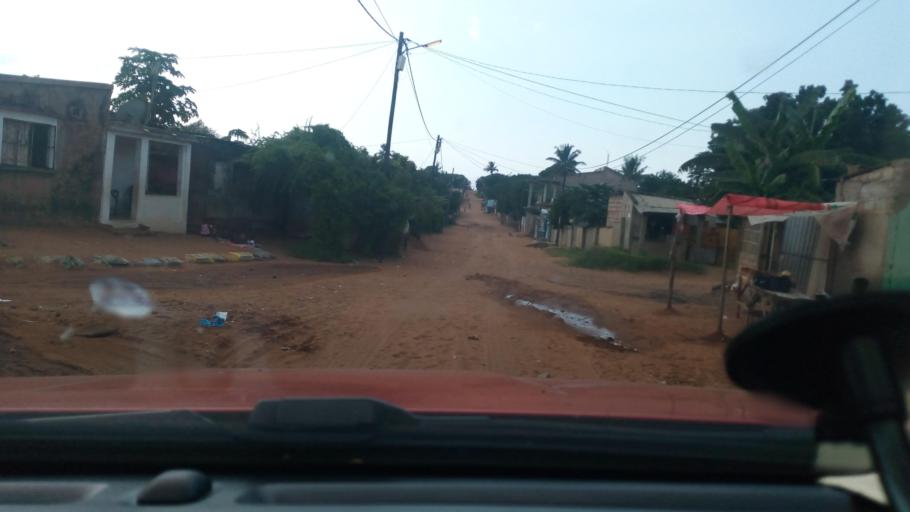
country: MZ
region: Maputo City
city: Maputo
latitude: -25.9211
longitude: 32.5960
